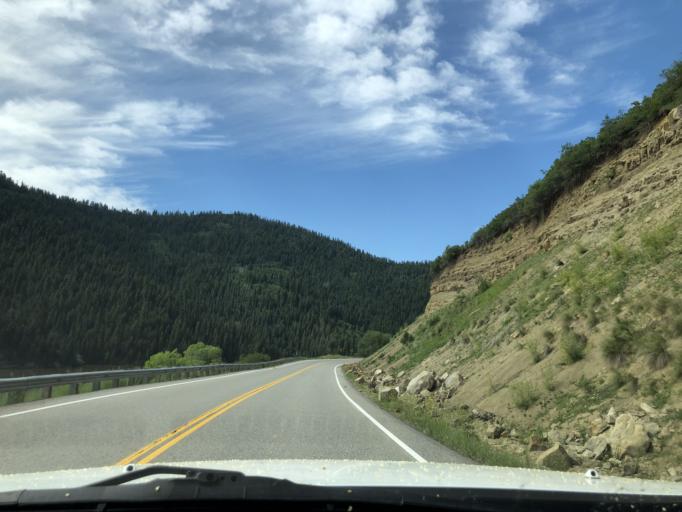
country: US
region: Colorado
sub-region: Delta County
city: Paonia
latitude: 38.9511
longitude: -107.3452
